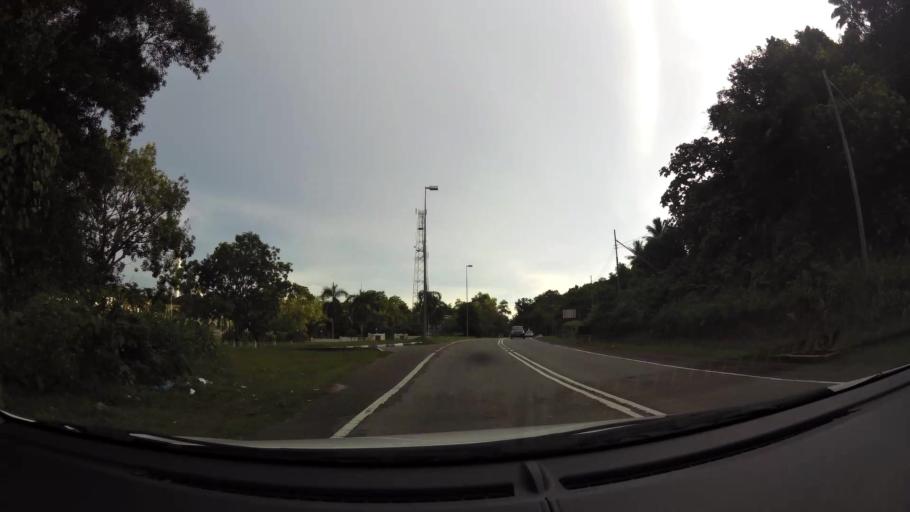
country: BN
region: Brunei and Muara
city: Bandar Seri Begawan
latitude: 4.9097
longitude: 114.9990
